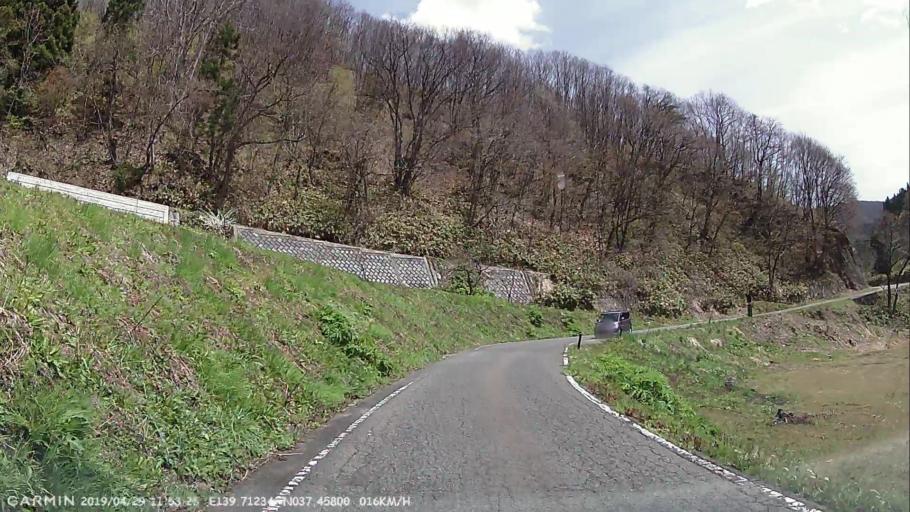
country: JP
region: Fukushima
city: Kitakata
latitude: 37.4580
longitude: 139.7123
